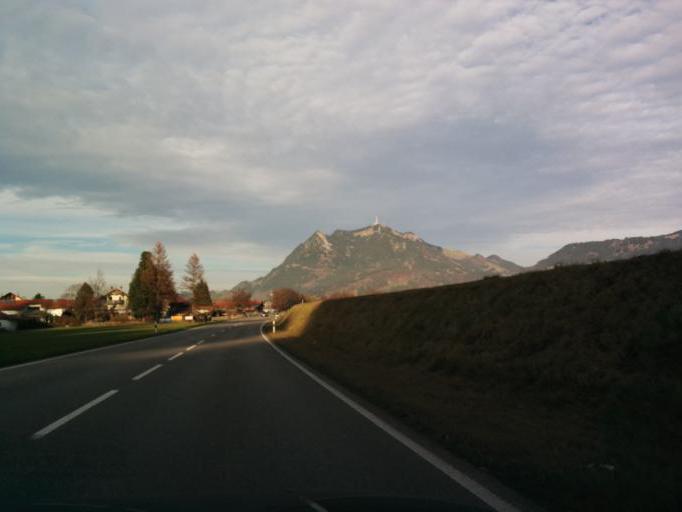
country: DE
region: Bavaria
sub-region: Swabia
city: Sonthofen
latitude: 47.5009
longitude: 10.2666
